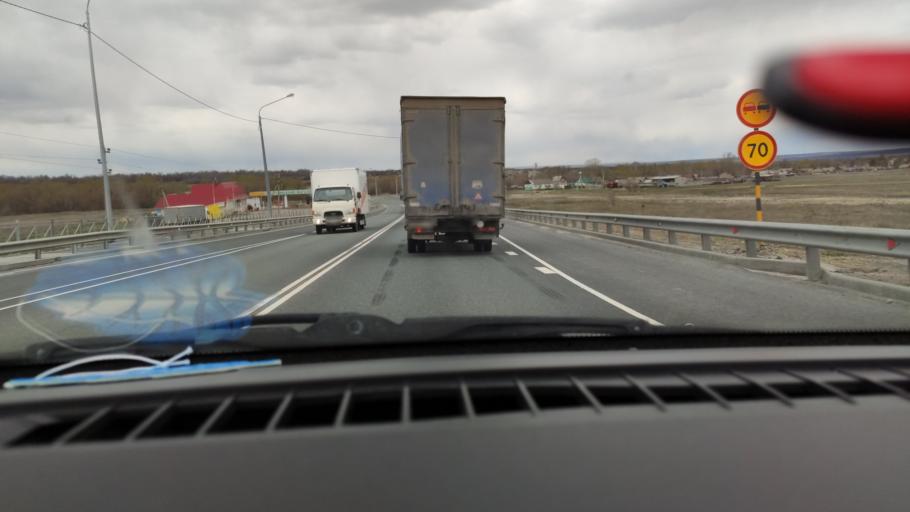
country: RU
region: Saratov
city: Sennoy
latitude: 52.1591
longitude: 47.0772
